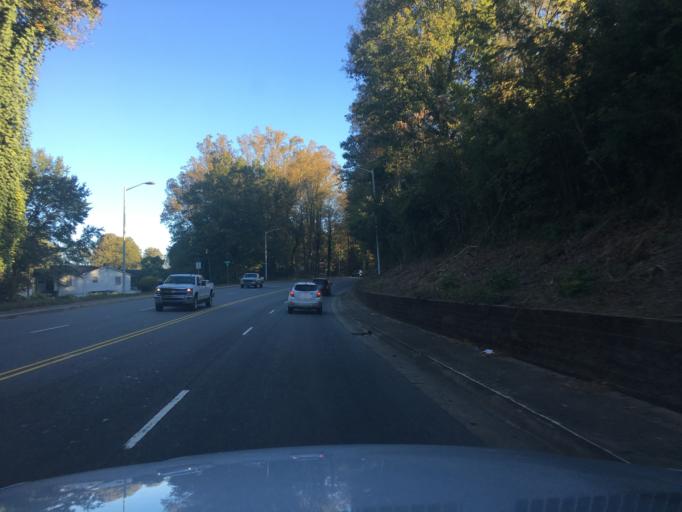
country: US
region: North Carolina
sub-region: Catawba County
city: Hickory
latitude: 35.7256
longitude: -81.3362
